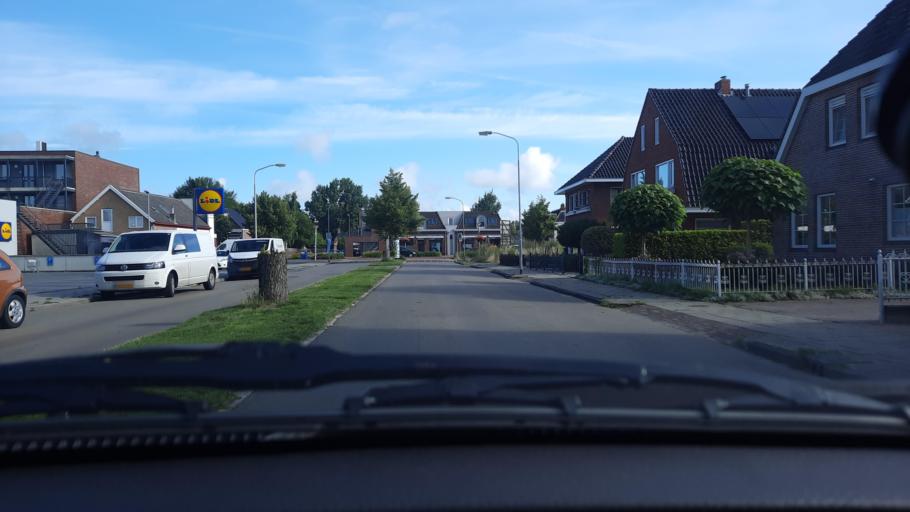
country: NL
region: Groningen
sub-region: Gemeente Hoogezand-Sappemeer
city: Sappemeer
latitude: 53.1633
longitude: 6.7862
